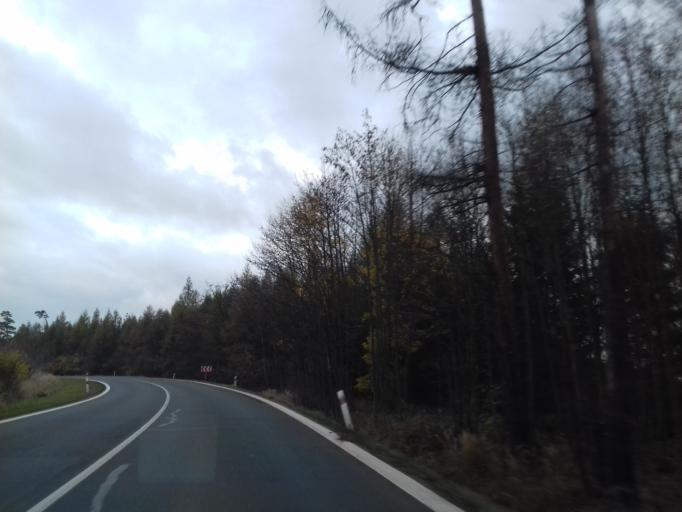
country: CZ
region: Pardubicky
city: Pomezi
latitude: 49.7399
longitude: 16.3815
